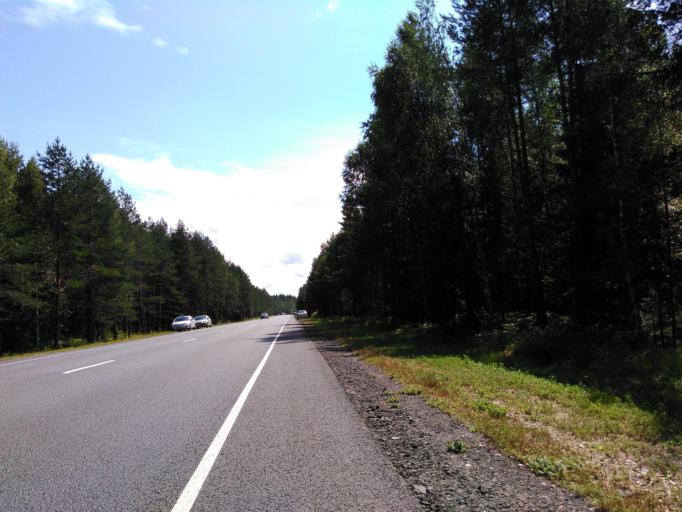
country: RU
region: Moskovskaya
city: Elektrogorsk
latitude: 56.0287
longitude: 38.7546
